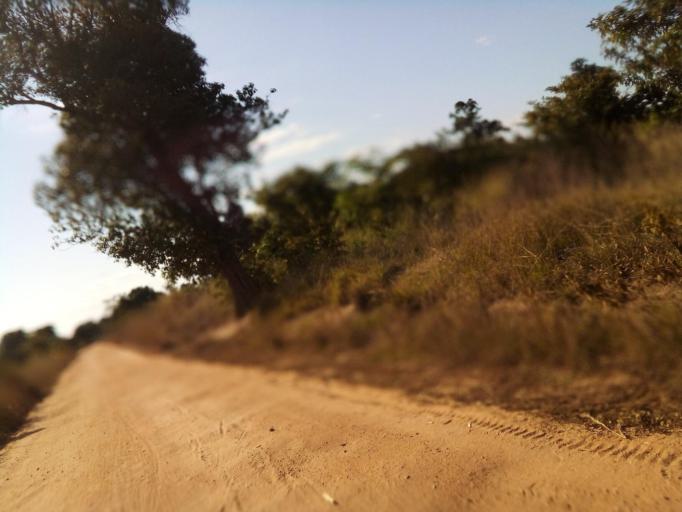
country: MZ
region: Zambezia
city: Quelimane
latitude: -17.5472
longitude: 36.6281
